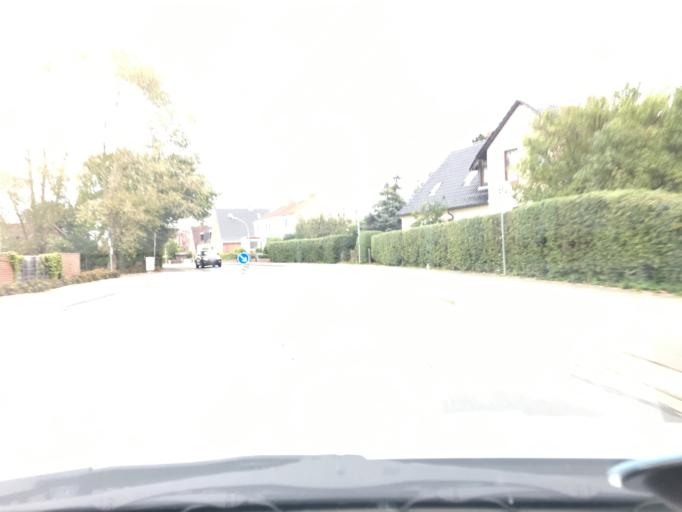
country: DE
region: Schleswig-Holstein
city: Kronshagen
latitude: 54.3370
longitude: 10.0778
